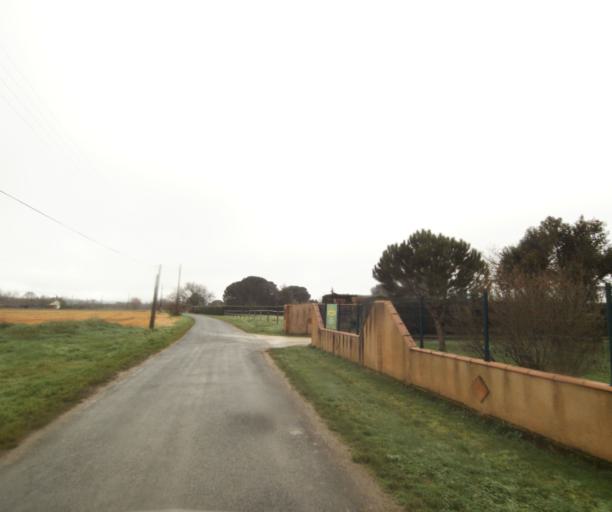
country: FR
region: Midi-Pyrenees
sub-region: Departement du Tarn-et-Garonne
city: Nohic
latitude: 43.8804
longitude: 1.4603
